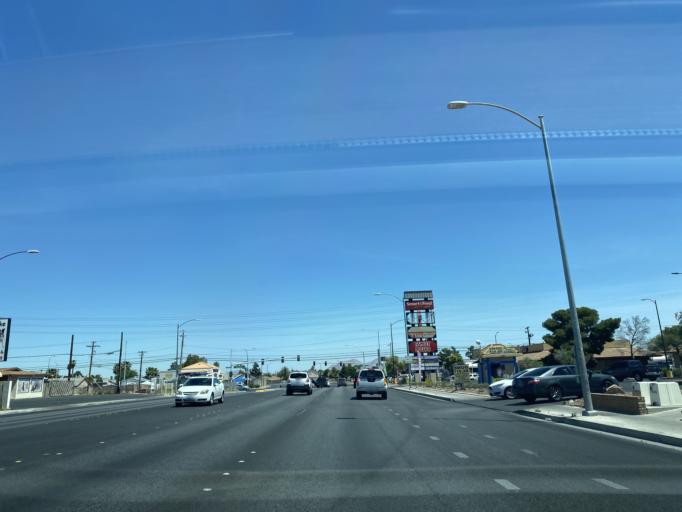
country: US
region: Nevada
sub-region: Clark County
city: Las Vegas
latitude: 36.1954
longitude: -115.2077
